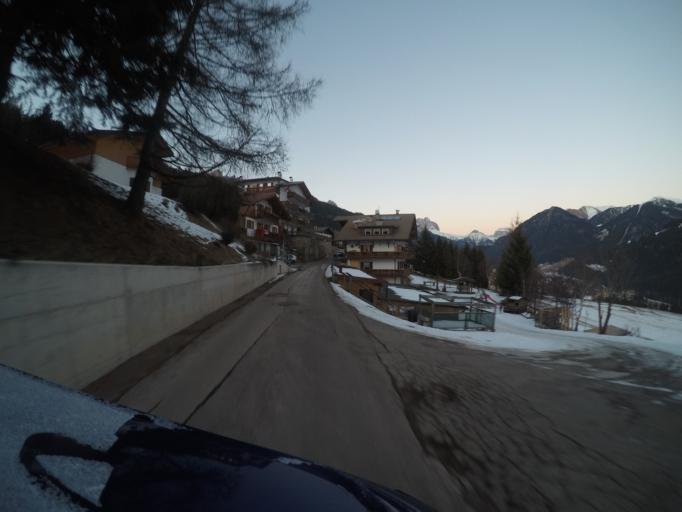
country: IT
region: Trentino-Alto Adige
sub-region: Provincia di Trento
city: Vigo di Fassa
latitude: 46.4140
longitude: 11.6686
